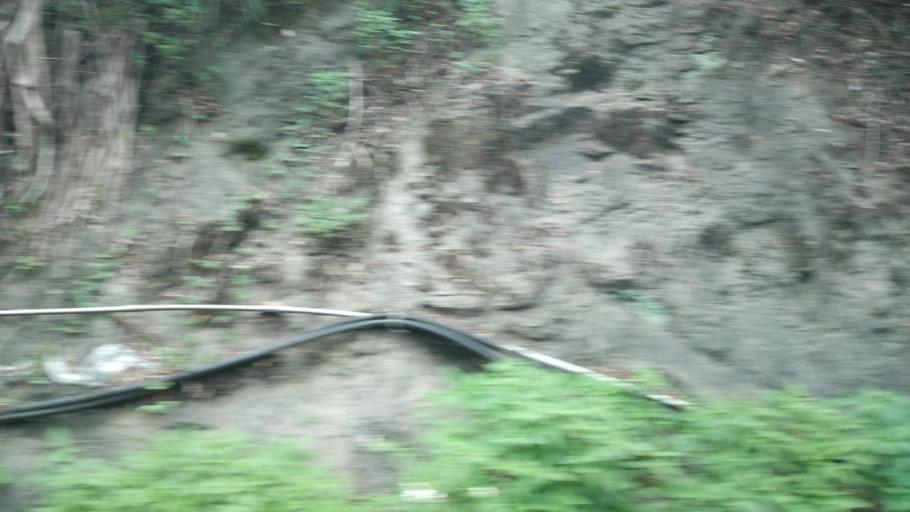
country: TW
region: Taipei
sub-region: Taipei
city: Banqiao
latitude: 24.9258
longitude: 121.4377
